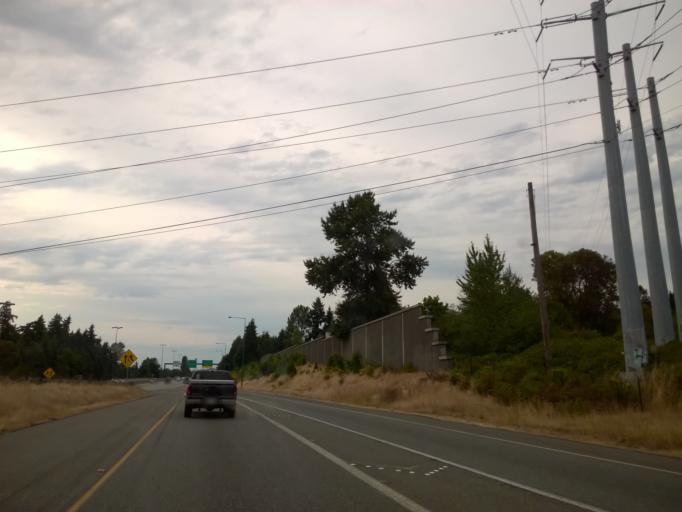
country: US
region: Washington
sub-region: King County
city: Newport
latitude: 47.5831
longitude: -122.1756
